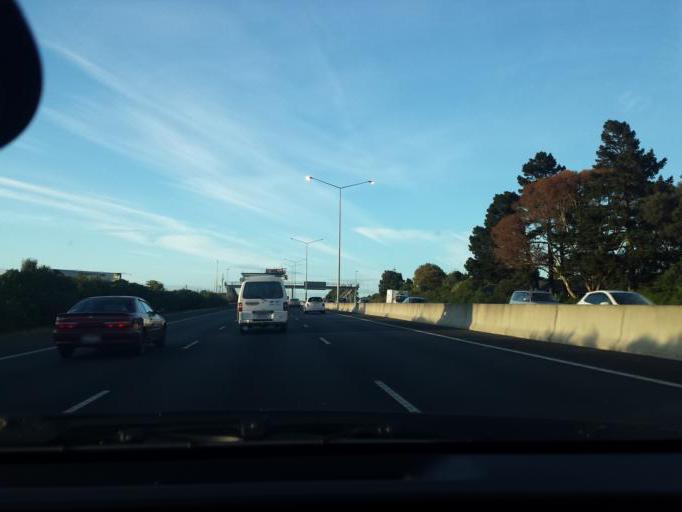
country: NZ
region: Auckland
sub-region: Auckland
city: Mangere
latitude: -36.9434
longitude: 174.7919
